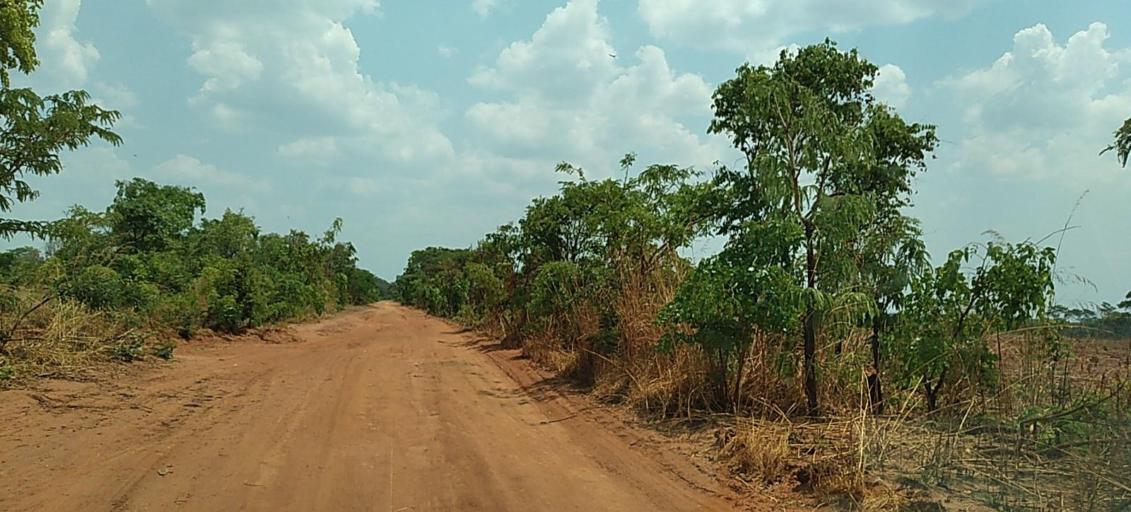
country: ZM
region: Copperbelt
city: Mpongwe
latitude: -13.6636
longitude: 28.0237
